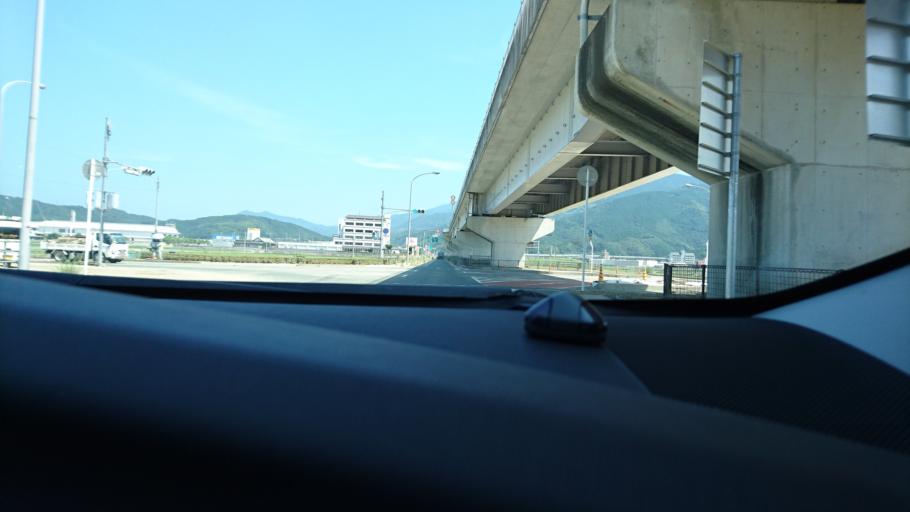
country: JP
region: Ehime
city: Ozu
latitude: 33.5239
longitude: 132.5763
